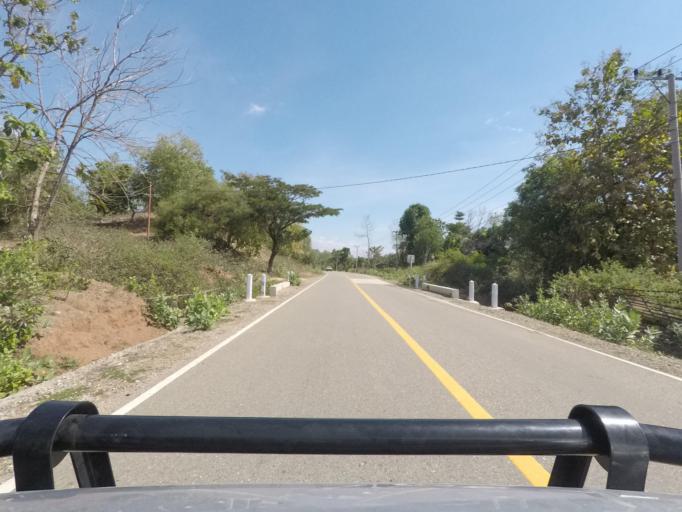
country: TL
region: Bobonaro
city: Maliana
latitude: -8.8769
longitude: 125.0387
